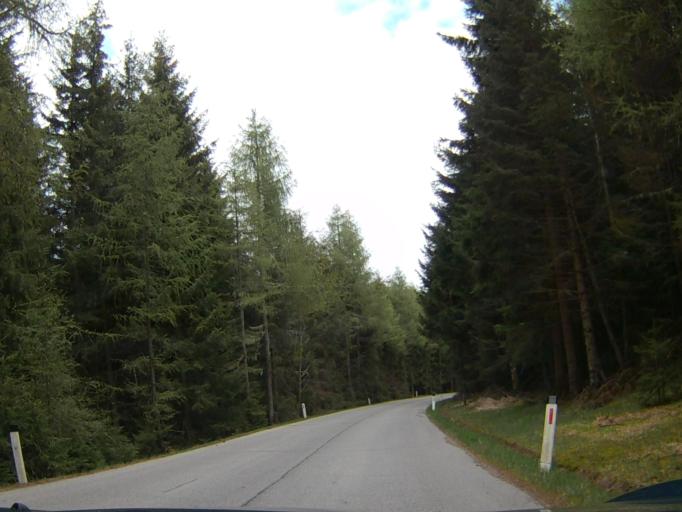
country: AT
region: Carinthia
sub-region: Politischer Bezirk Villach Land
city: Stockenboi
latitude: 46.7419
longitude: 13.5372
